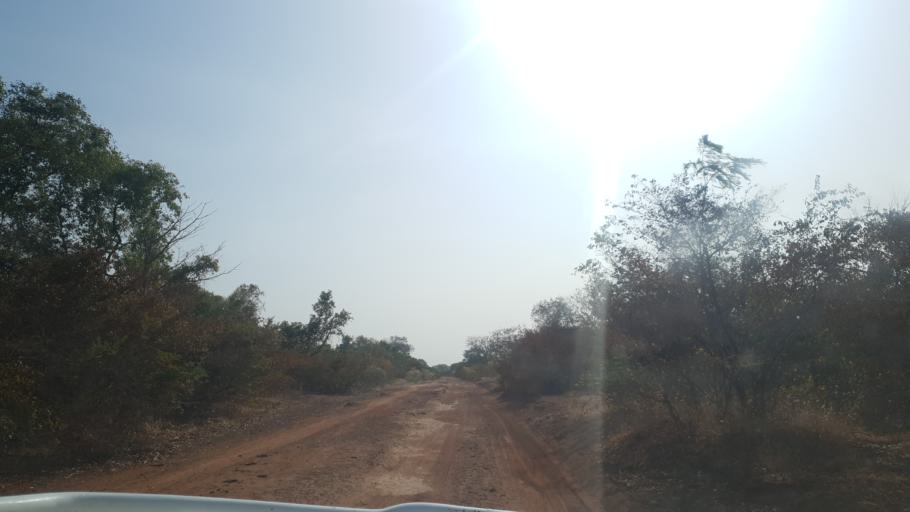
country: ML
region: Koulikoro
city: Dioila
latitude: 12.7102
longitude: -6.7856
